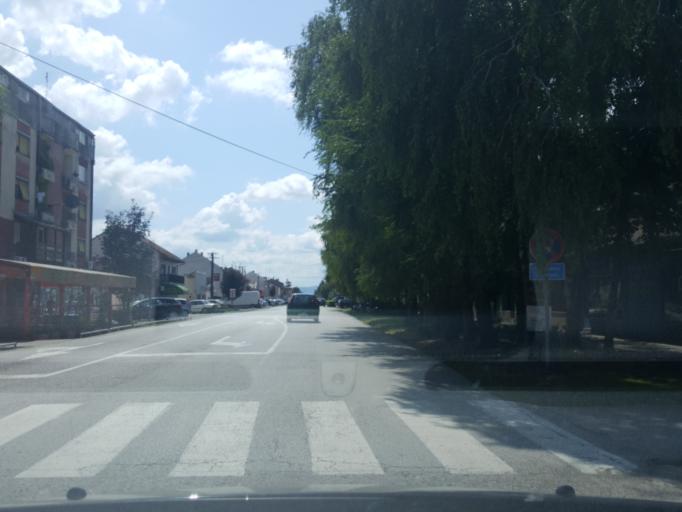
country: RS
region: Central Serbia
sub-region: Macvanski Okrug
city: Bogatic
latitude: 44.8343
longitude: 19.4796
